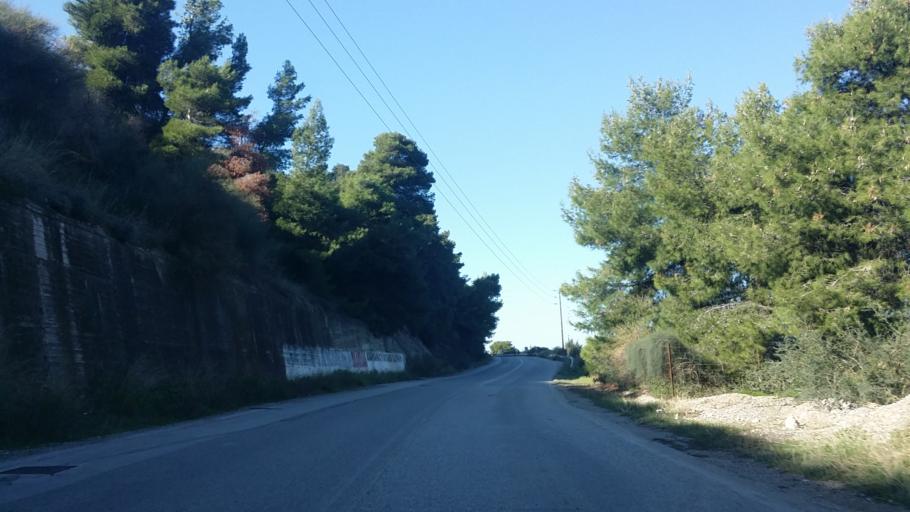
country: GR
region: West Greece
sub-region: Nomos Achaias
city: Akrata
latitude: 38.1800
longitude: 22.2151
